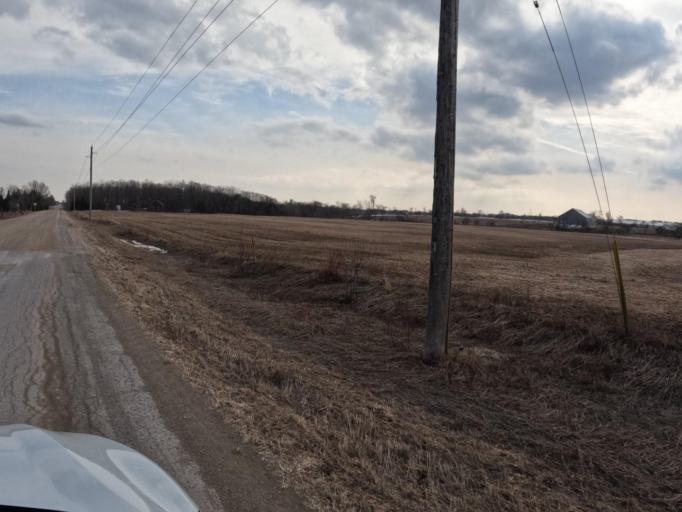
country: CA
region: Ontario
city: Shelburne
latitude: 43.9261
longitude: -80.3073
